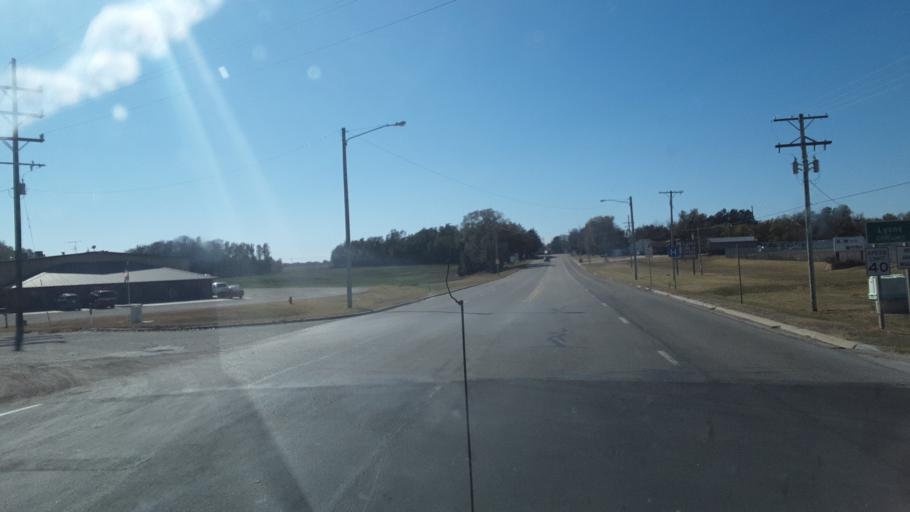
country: US
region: Kansas
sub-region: Rice County
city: Lyons
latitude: 38.3527
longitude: -98.1833
